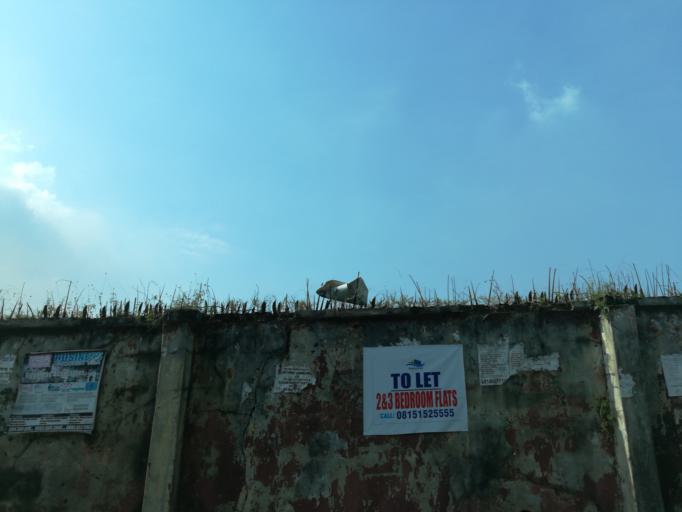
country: NG
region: Rivers
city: Port Harcourt
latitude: 4.8309
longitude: 6.9944
